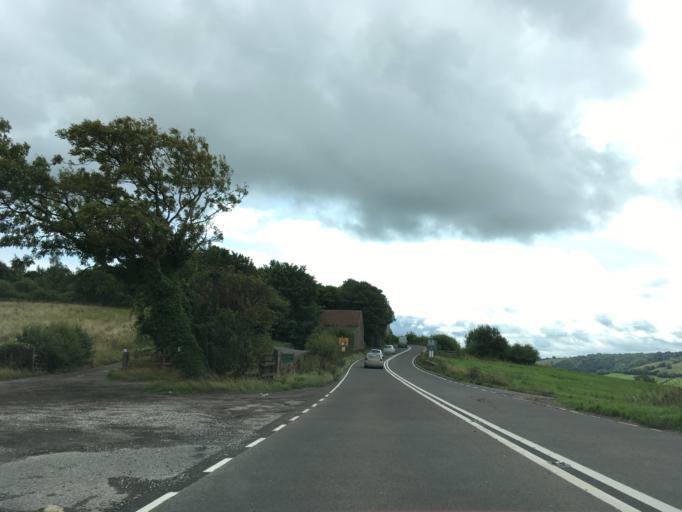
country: GB
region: England
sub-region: South Gloucestershire
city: Cold Ashton
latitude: 51.4350
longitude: -2.3670
